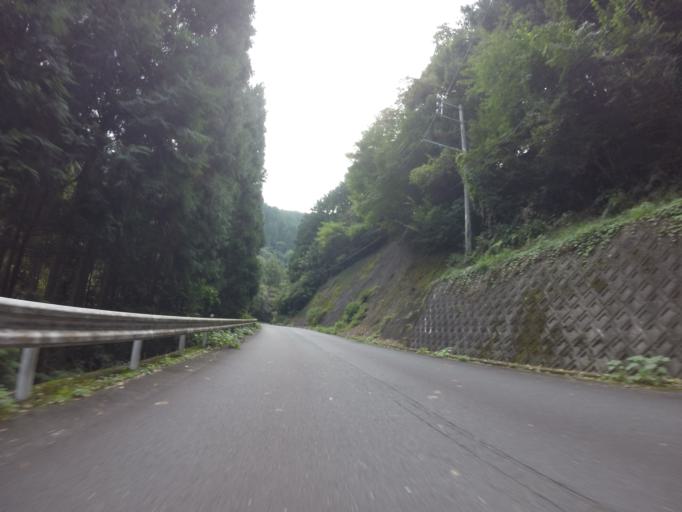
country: JP
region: Shizuoka
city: Mori
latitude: 34.8756
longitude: 138.0248
